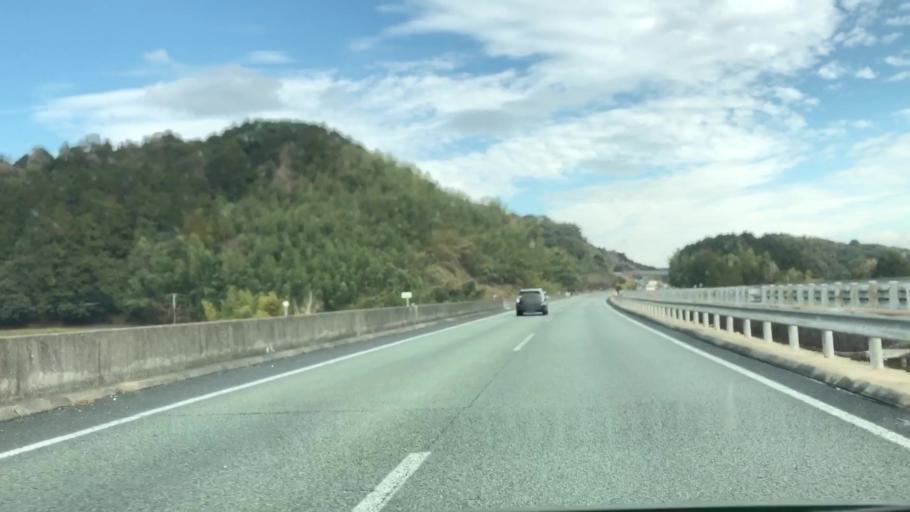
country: JP
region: Saga Prefecture
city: Tosu
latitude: 33.3885
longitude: 130.4860
